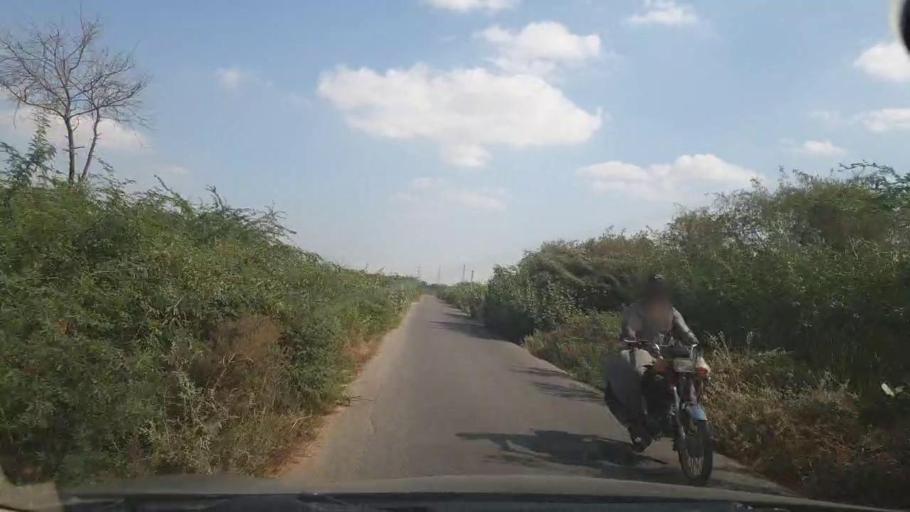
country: PK
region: Sindh
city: Malir Cantonment
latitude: 25.0170
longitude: 67.3550
